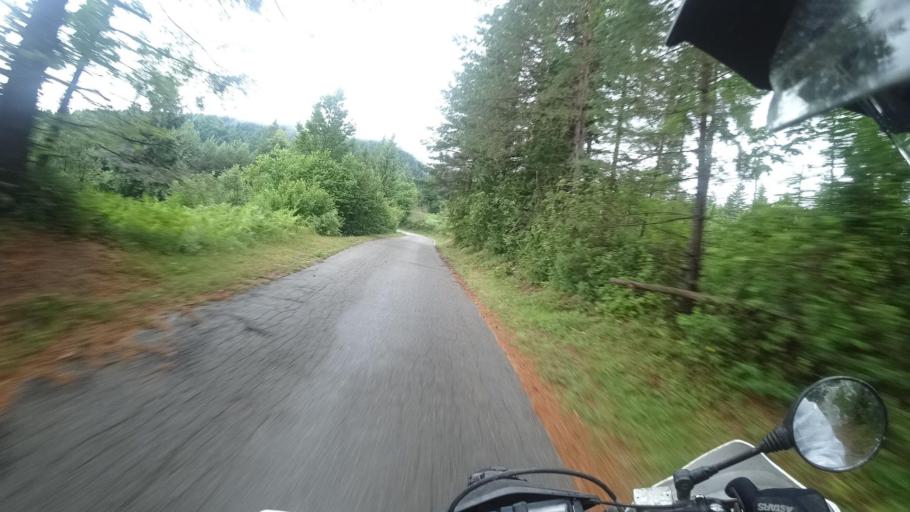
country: HR
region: Karlovacka
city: Plaski
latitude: 44.9994
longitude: 15.4148
